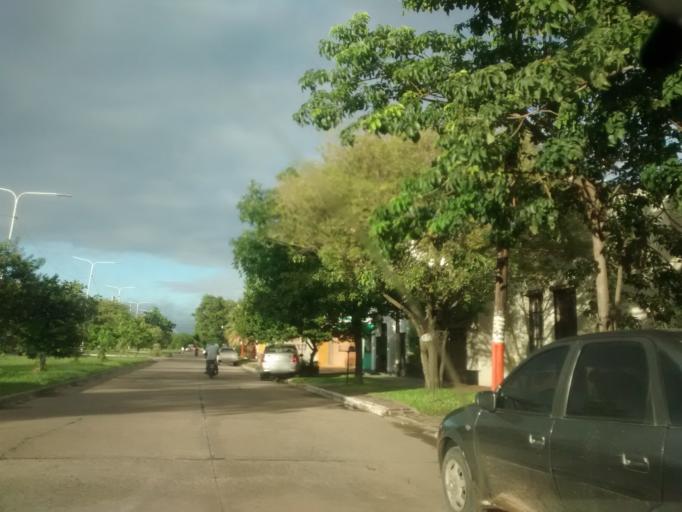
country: AR
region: Chaco
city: Resistencia
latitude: -27.4661
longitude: -58.9893
